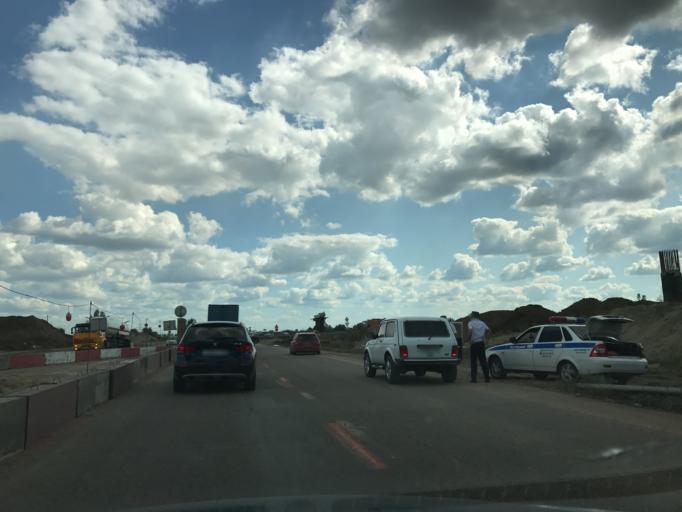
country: RU
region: Adygeya
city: Tlyustenkhabl'
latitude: 44.9504
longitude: 39.1240
